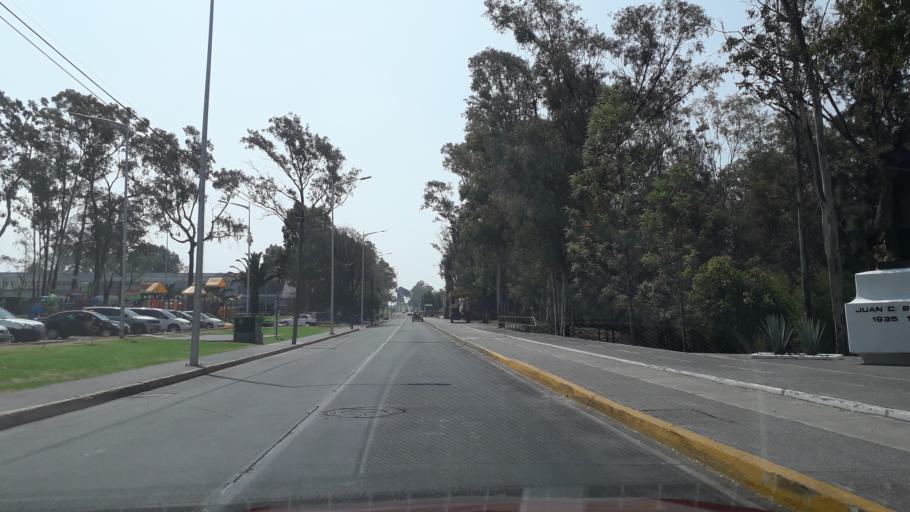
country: MX
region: Puebla
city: Puebla
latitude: 19.0572
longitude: -98.1843
